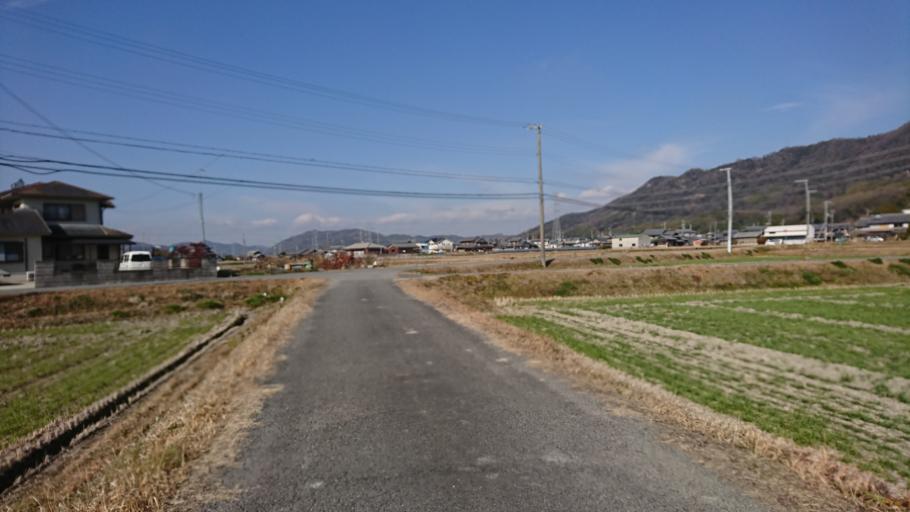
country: JP
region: Hyogo
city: Kakogawacho-honmachi
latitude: 34.8191
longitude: 134.8504
